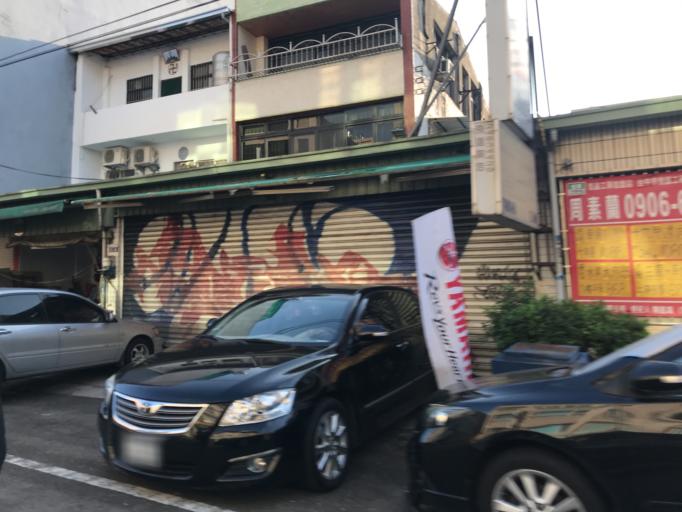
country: TW
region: Taiwan
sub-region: Taichung City
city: Taichung
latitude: 24.1204
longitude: 120.6925
